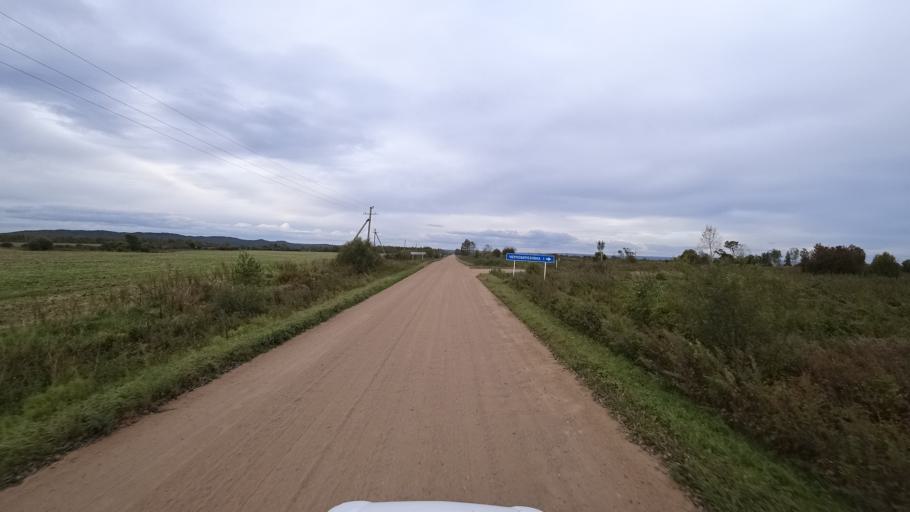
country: RU
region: Amur
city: Arkhara
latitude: 49.4365
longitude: 130.2566
